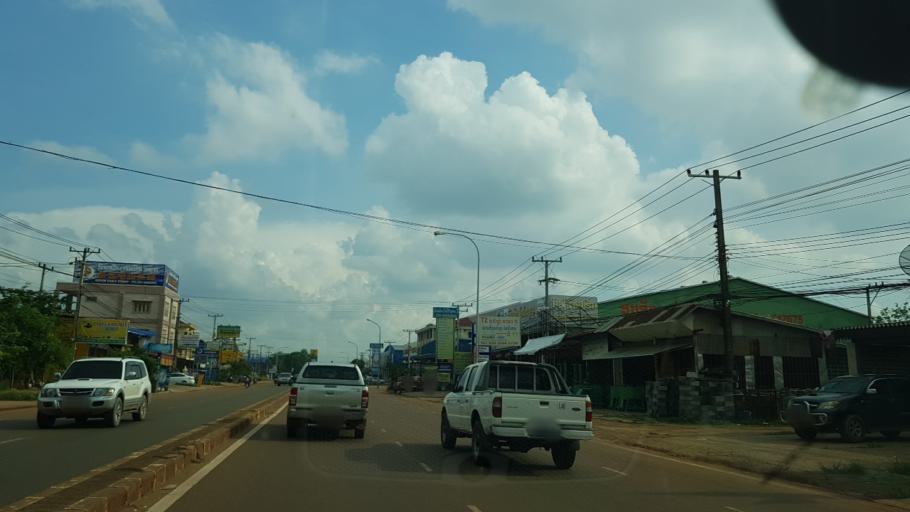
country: LA
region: Vientiane
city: Vientiane
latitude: 18.0223
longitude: 102.6515
